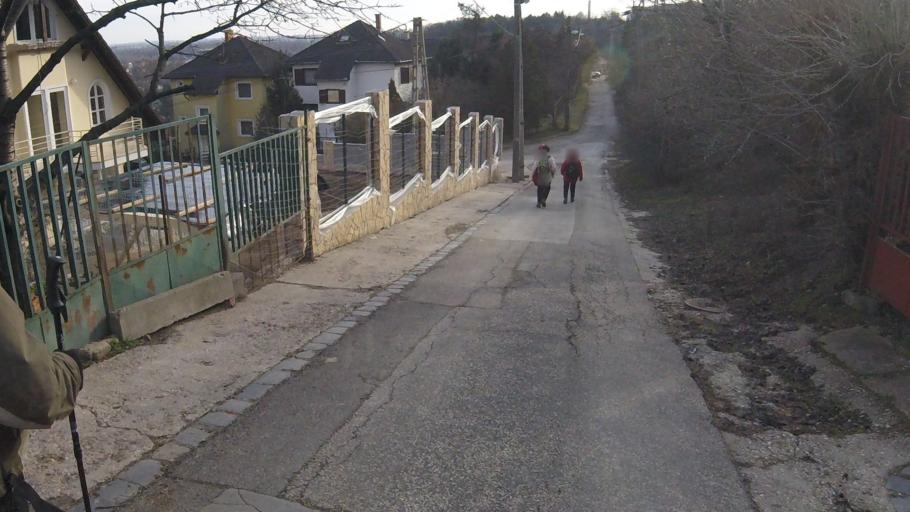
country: HU
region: Pest
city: Urom
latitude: 47.5914
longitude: 19.0388
